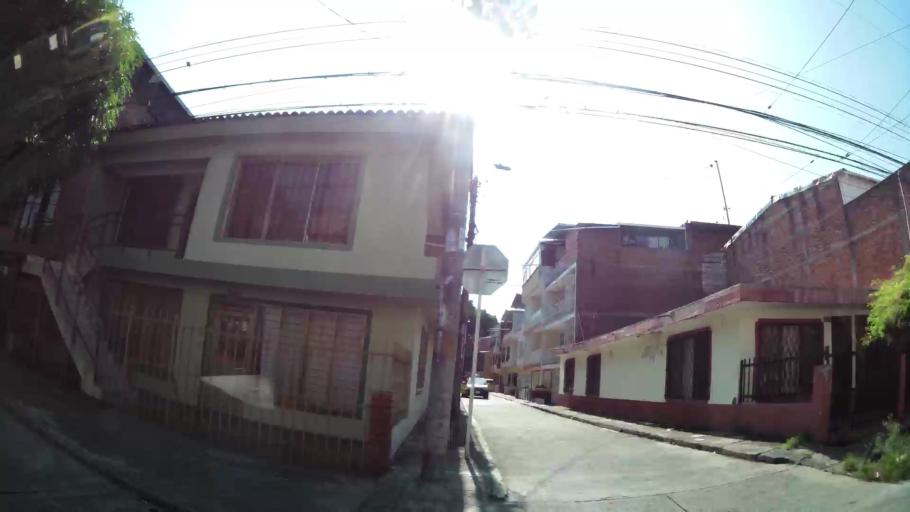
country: CO
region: Valle del Cauca
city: Cali
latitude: 3.4104
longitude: -76.5267
